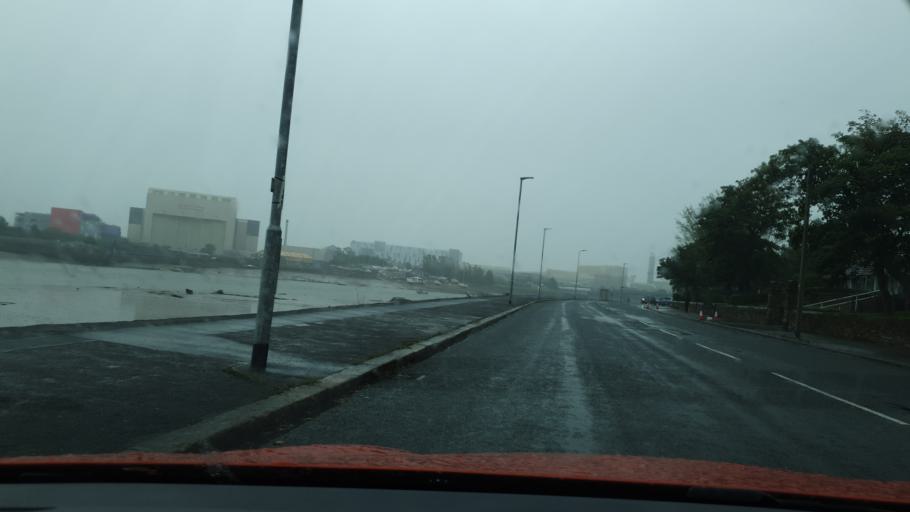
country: GB
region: England
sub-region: Cumbria
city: Barrow in Furness
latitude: 54.1122
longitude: -3.2479
